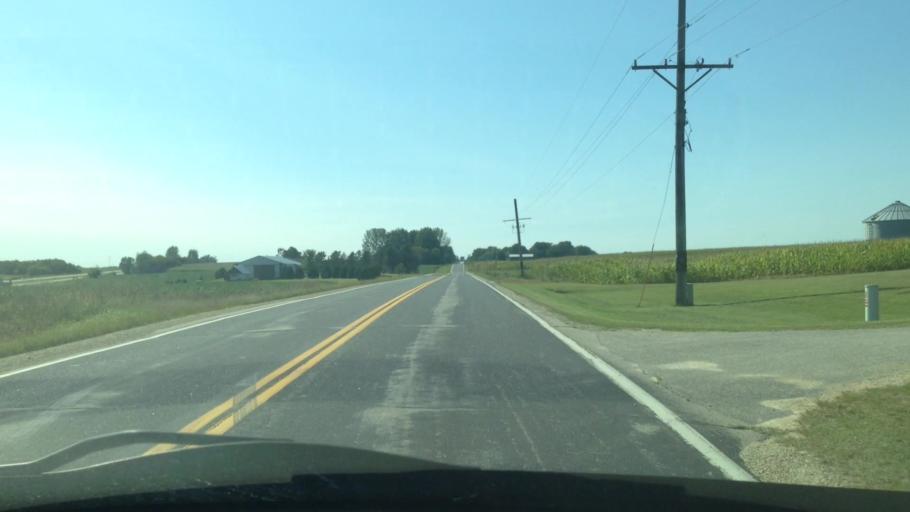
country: US
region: Minnesota
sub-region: Winona County
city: Lewiston
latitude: 43.9404
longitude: -91.7778
